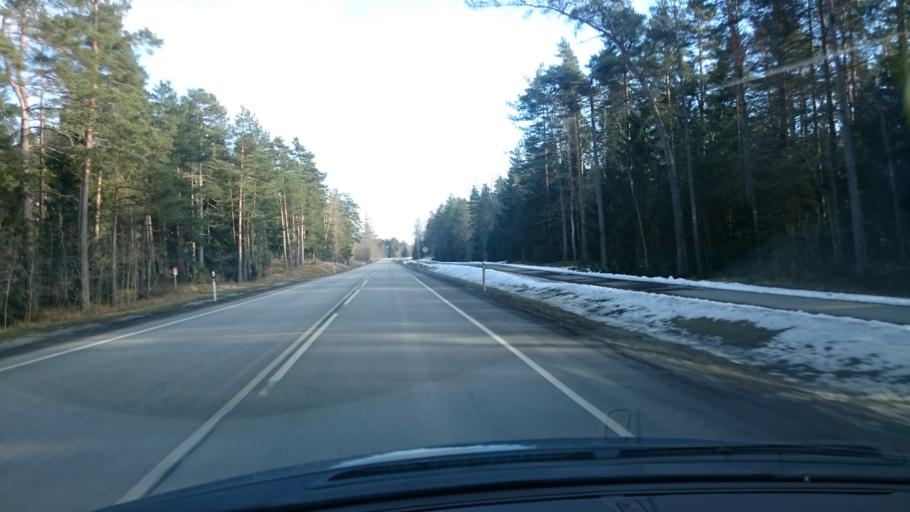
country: EE
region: Harju
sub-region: Kiili vald
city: Kiili
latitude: 59.3528
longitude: 24.7862
